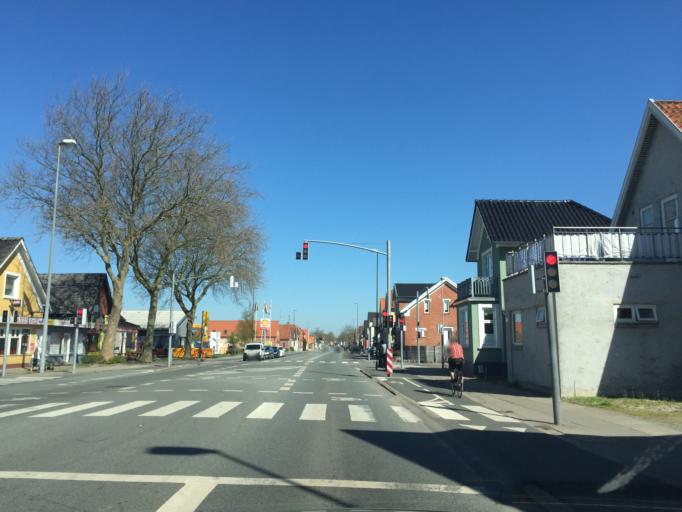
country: DK
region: South Denmark
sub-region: Odense Kommune
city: Odense
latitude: 55.3680
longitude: 10.3726
